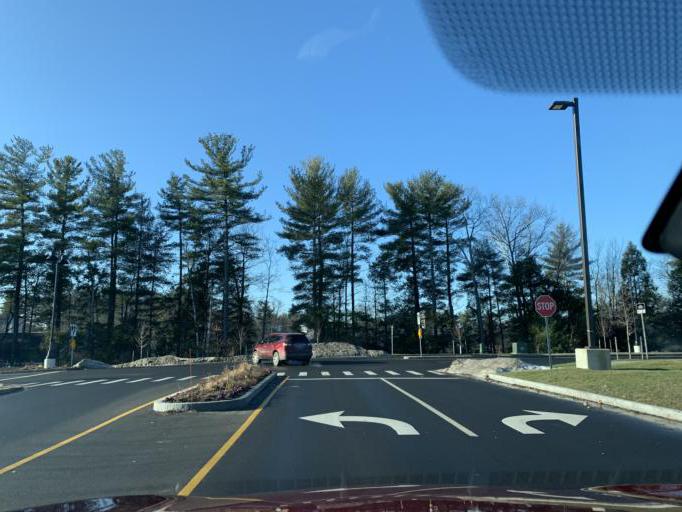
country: US
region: New Hampshire
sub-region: Rockingham County
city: Derry
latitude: 42.8696
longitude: -71.3488
